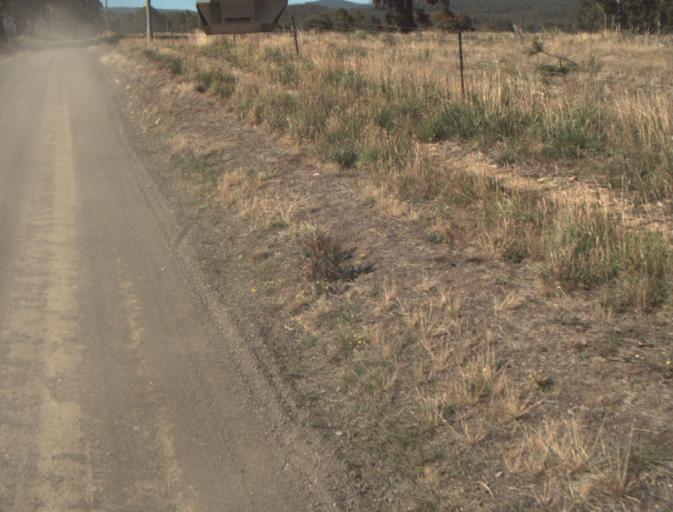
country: AU
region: Tasmania
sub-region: Launceston
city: Newstead
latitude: -41.3100
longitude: 147.3202
